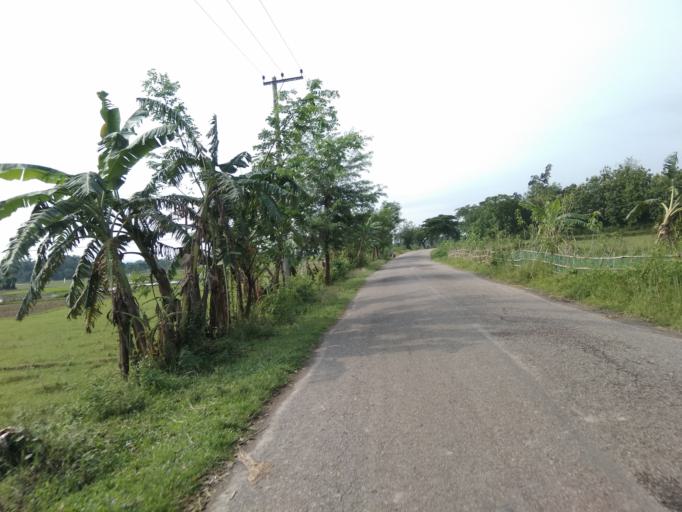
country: BD
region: Chittagong
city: Khagrachhari
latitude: 23.0239
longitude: 92.0149
